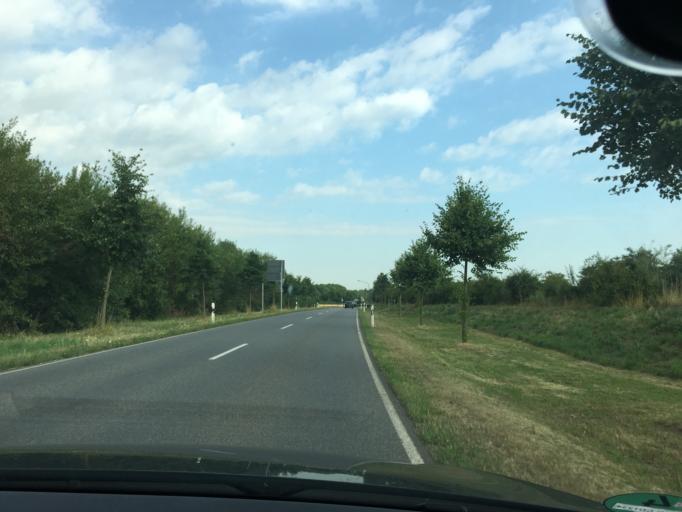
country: DE
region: North Rhine-Westphalia
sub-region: Regierungsbezirk Koln
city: Inden
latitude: 50.8716
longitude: 6.4002
